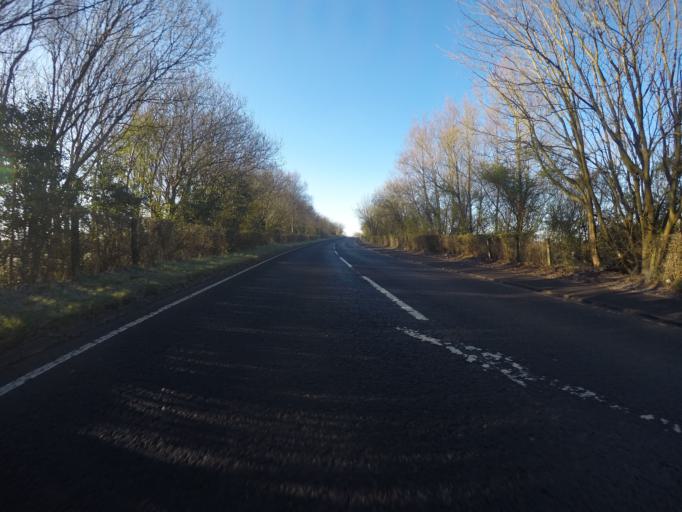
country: GB
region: Scotland
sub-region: North Ayrshire
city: Stevenston
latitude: 55.6391
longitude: -4.7403
